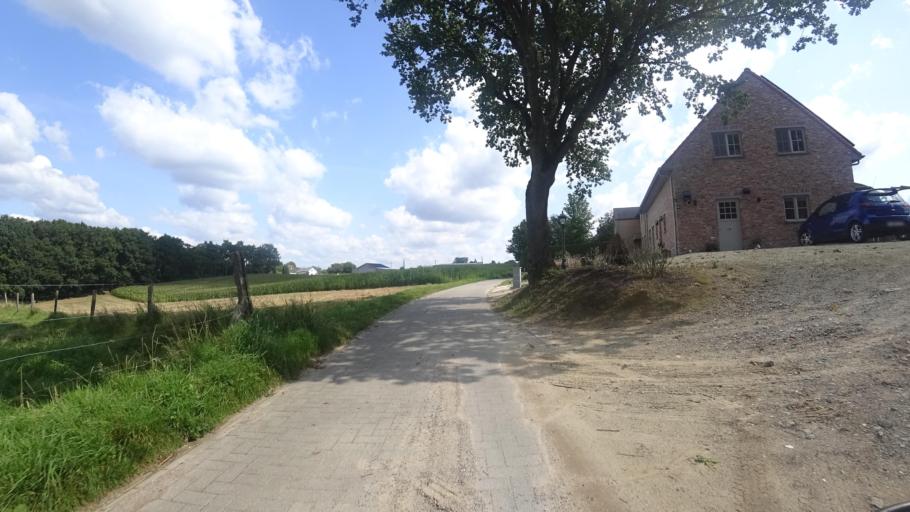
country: BE
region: Wallonia
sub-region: Province du Brabant Wallon
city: Wavre
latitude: 50.7586
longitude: 4.6151
